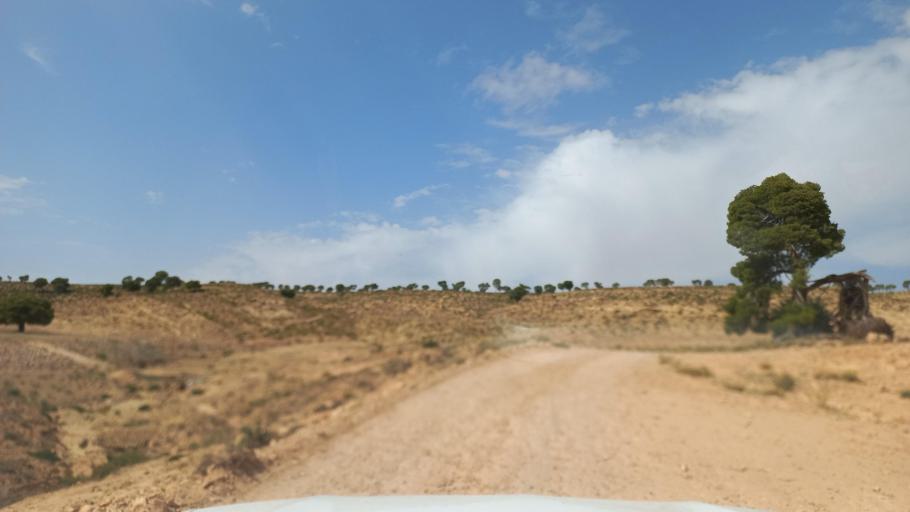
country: TN
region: Al Qasrayn
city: Kasserine
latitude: 35.3721
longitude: 8.8790
